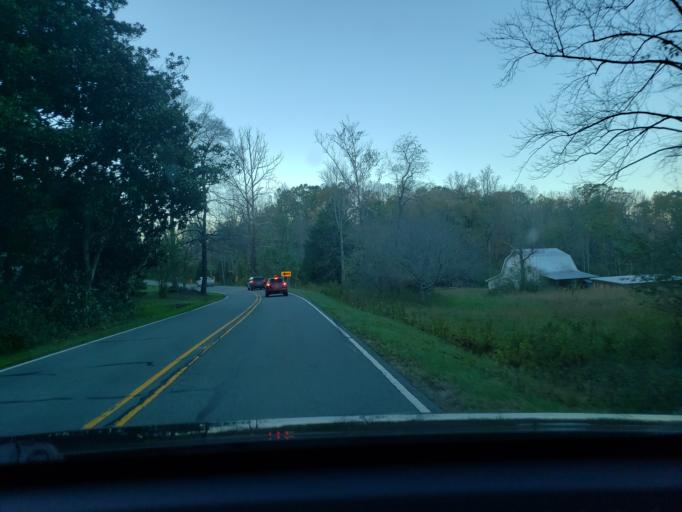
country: US
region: North Carolina
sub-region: Stokes County
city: Danbury
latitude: 36.4230
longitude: -80.2360
